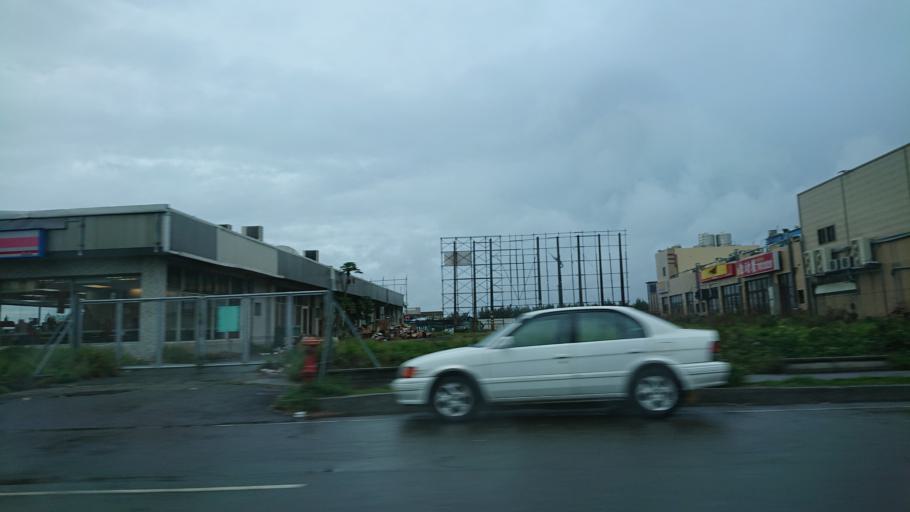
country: TW
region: Taiwan
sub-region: Changhua
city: Chang-hua
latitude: 24.0769
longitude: 120.4113
